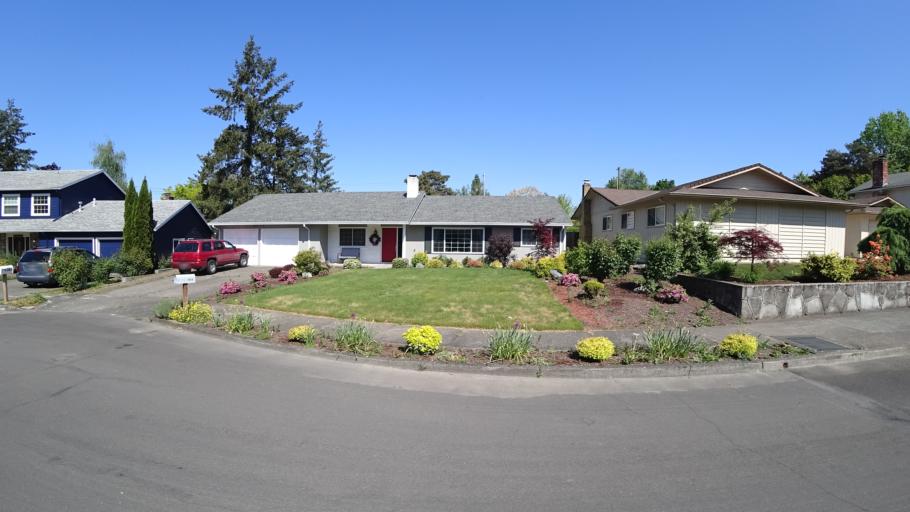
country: US
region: Oregon
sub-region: Washington County
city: Bethany
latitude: 45.5554
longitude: -122.8686
